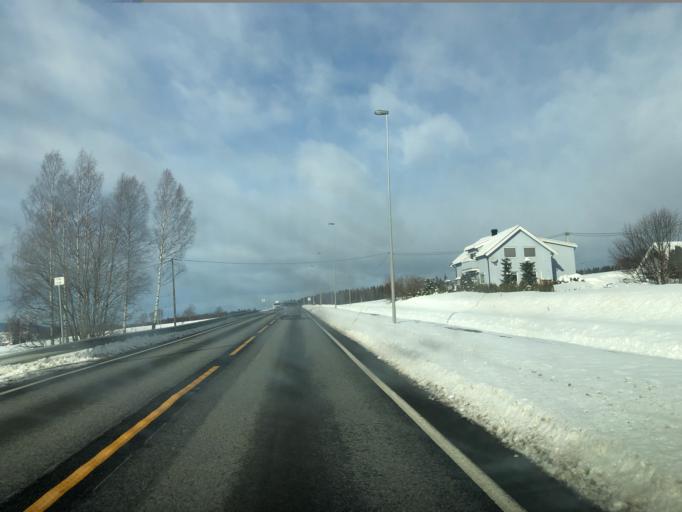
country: NO
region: Oppland
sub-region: Vestre Toten
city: Reinsvoll
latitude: 60.5464
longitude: 10.6585
